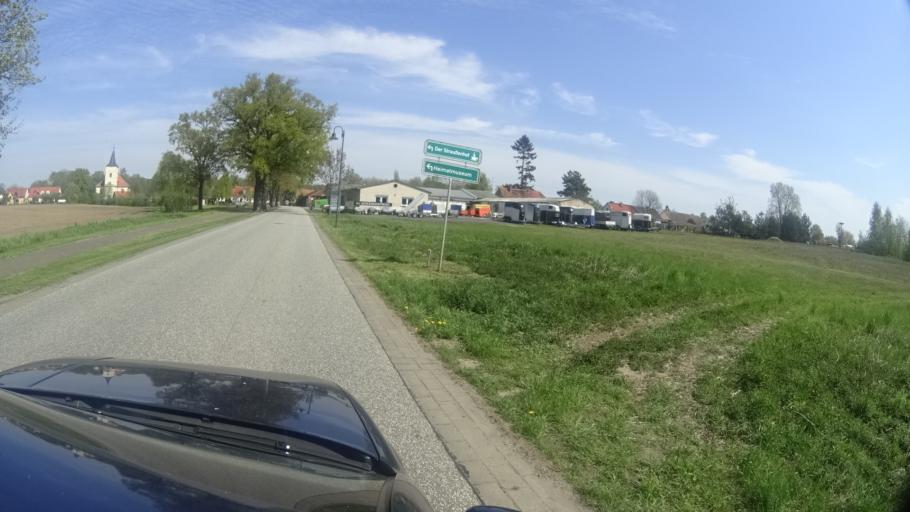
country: DE
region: Brandenburg
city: Grossderschau
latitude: 52.7894
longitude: 12.3677
